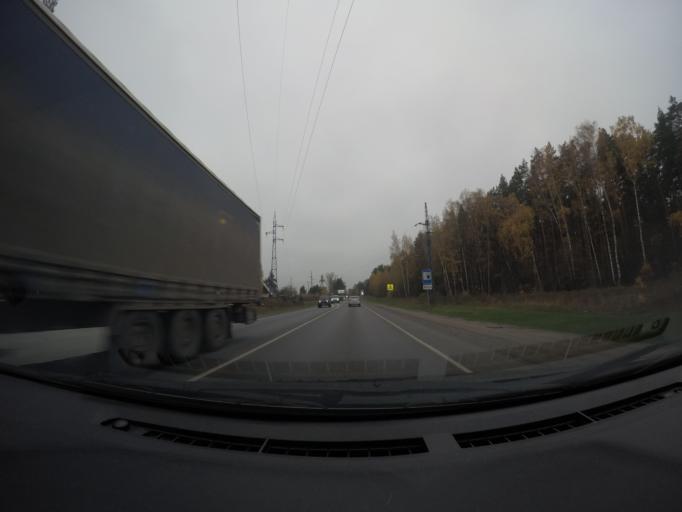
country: RU
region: Moskovskaya
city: Malyshevo
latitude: 55.4758
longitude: 38.3446
